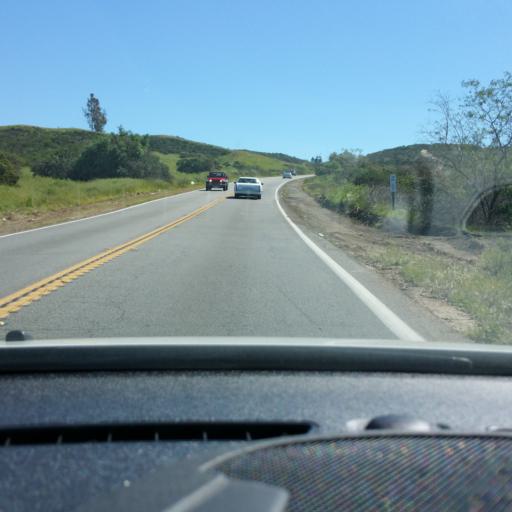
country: US
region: California
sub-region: Riverside County
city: Temecula
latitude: 33.4794
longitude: -117.0342
